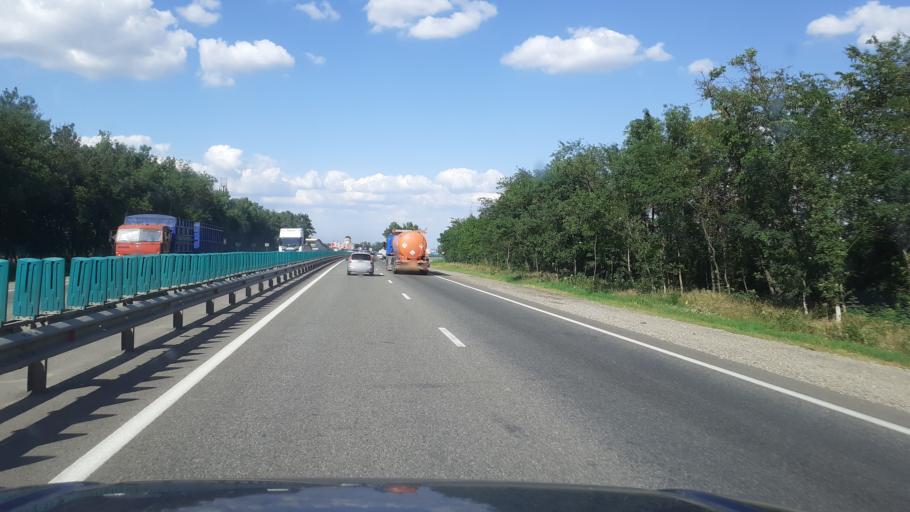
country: RU
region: Krasnodarskiy
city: Severskaya
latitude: 44.8521
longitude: 38.7073
